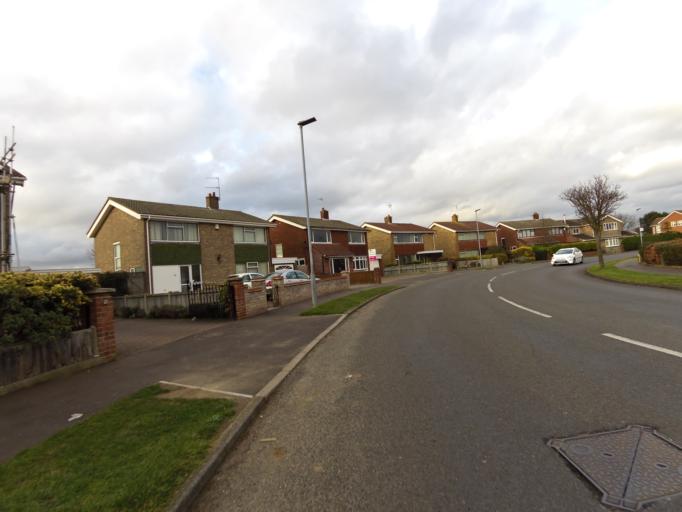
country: GB
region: England
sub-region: Norfolk
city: Gorleston-on-Sea
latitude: 52.5572
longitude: 1.7271
